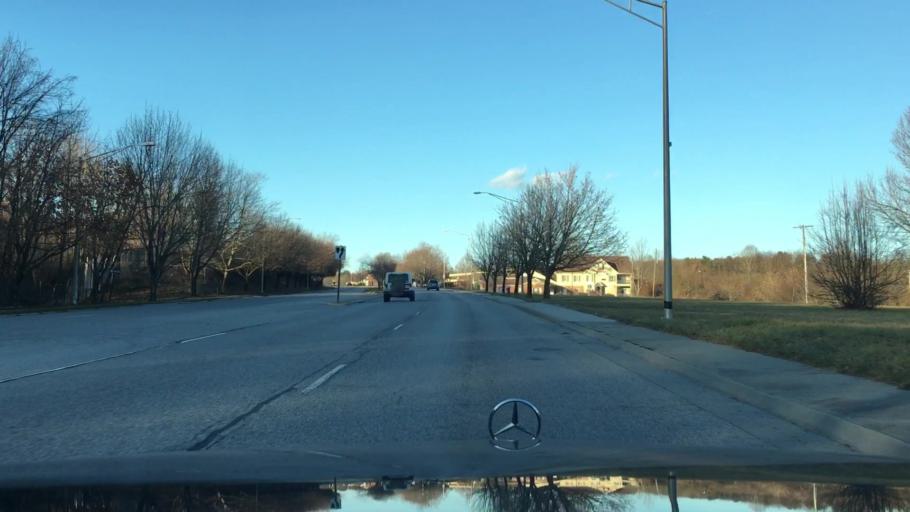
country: US
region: Virginia
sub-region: Montgomery County
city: Merrimac
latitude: 37.2033
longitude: -80.3991
